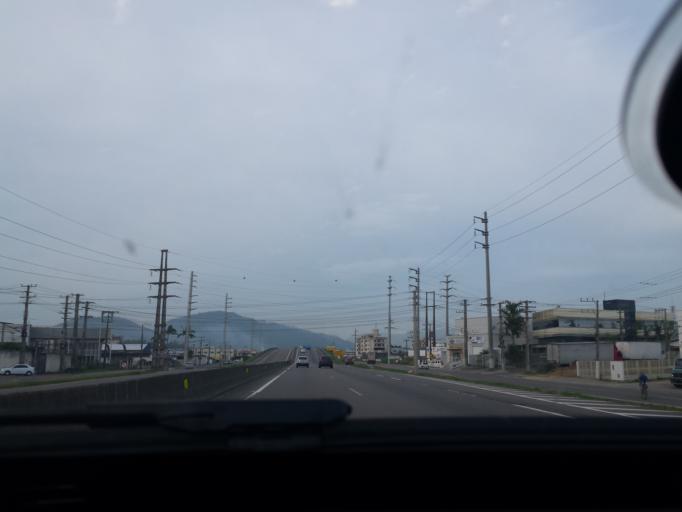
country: BR
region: Santa Catarina
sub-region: Tubarao
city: Tubarao
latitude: -28.4683
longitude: -49.0115
